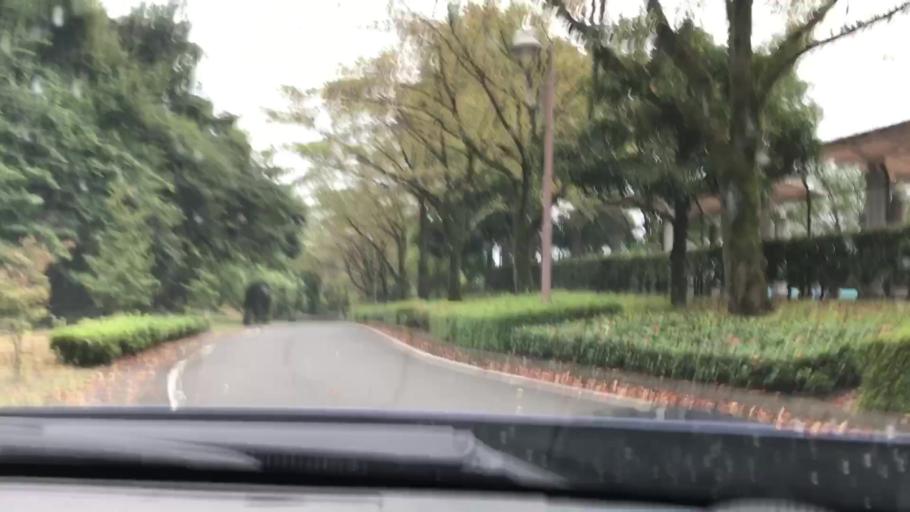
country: JP
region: Gunma
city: Kanekomachi
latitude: 36.3987
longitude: 138.9515
